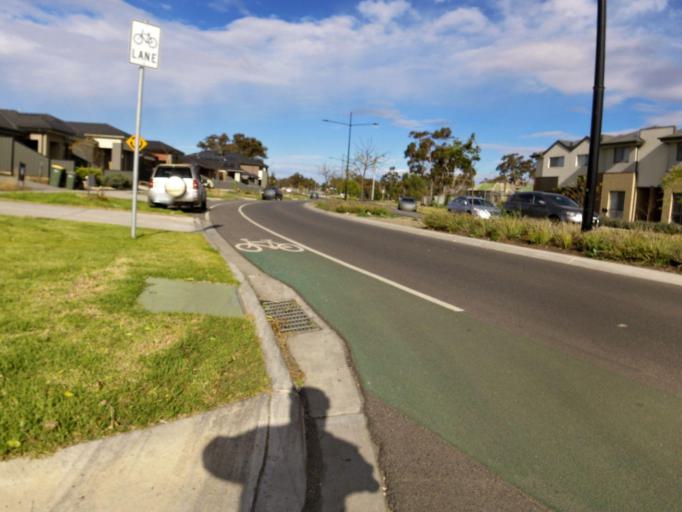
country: AU
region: Victoria
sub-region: Whittlesea
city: Epping
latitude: -37.6228
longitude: 145.0396
